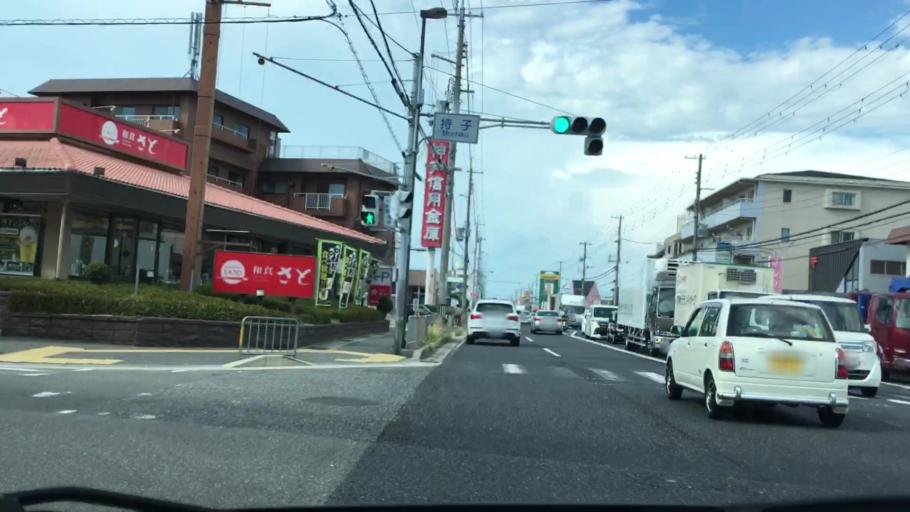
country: JP
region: Hyogo
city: Akashi
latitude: 34.6725
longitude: 134.9815
